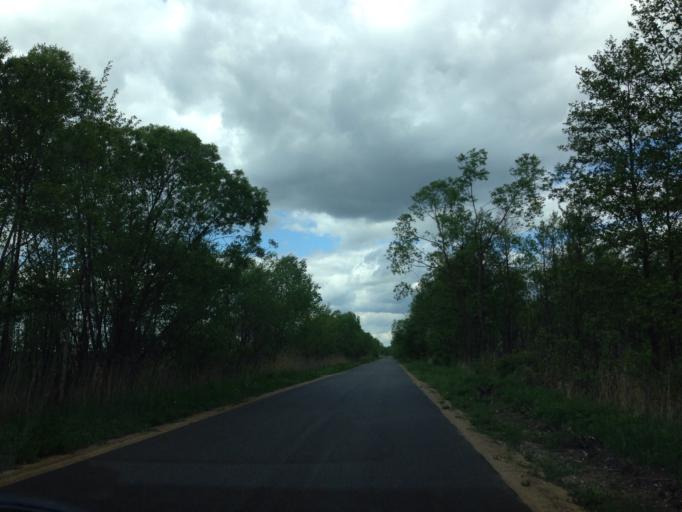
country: PL
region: Podlasie
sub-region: Powiat bialostocki
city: Tykocin
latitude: 53.2916
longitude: 22.6085
